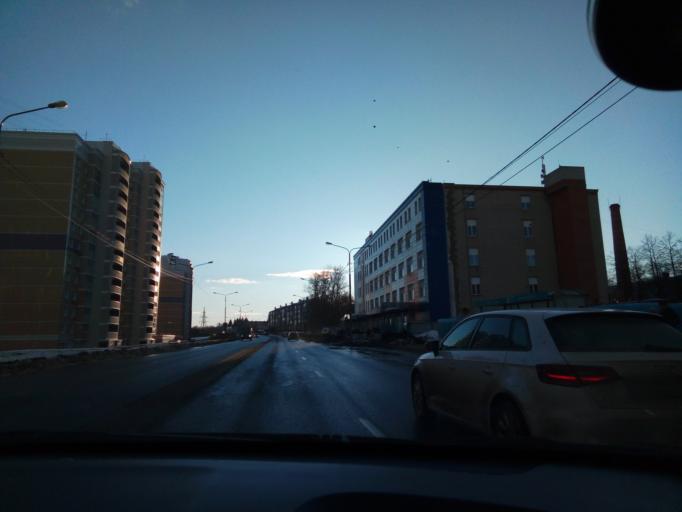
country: RU
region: Chuvashia
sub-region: Cheboksarskiy Rayon
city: Cheboksary
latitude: 56.1398
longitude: 47.2161
